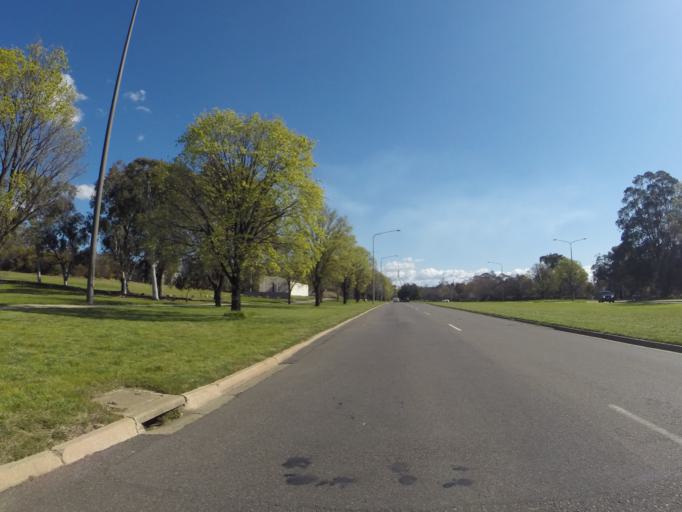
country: AU
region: Australian Capital Territory
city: Forrest
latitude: -35.3028
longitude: 149.1387
